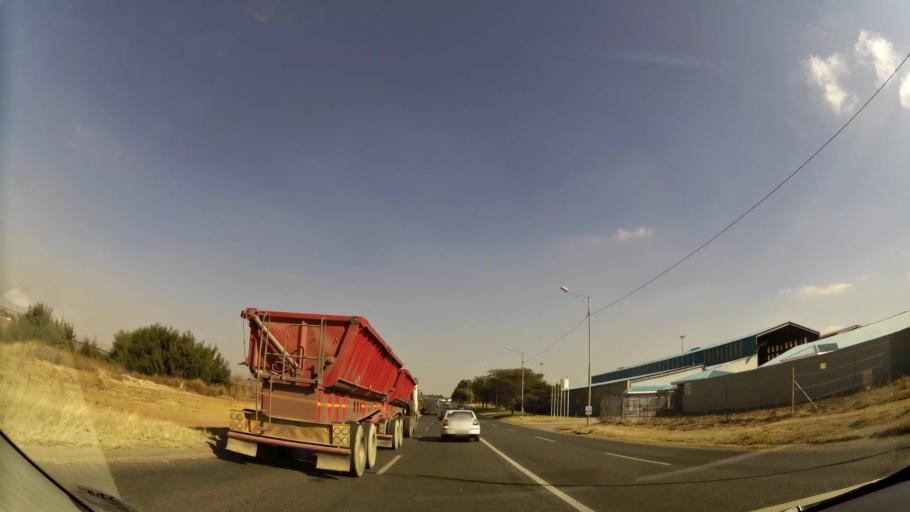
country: ZA
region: Gauteng
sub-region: City of Johannesburg Metropolitan Municipality
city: Roodepoort
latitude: -26.1504
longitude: 27.8112
